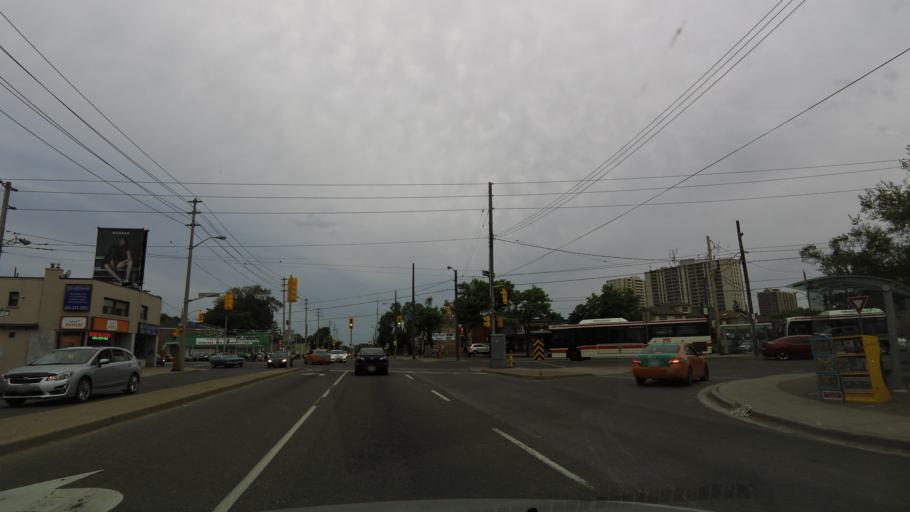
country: CA
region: Ontario
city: Etobicoke
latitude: 43.6919
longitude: -79.5011
